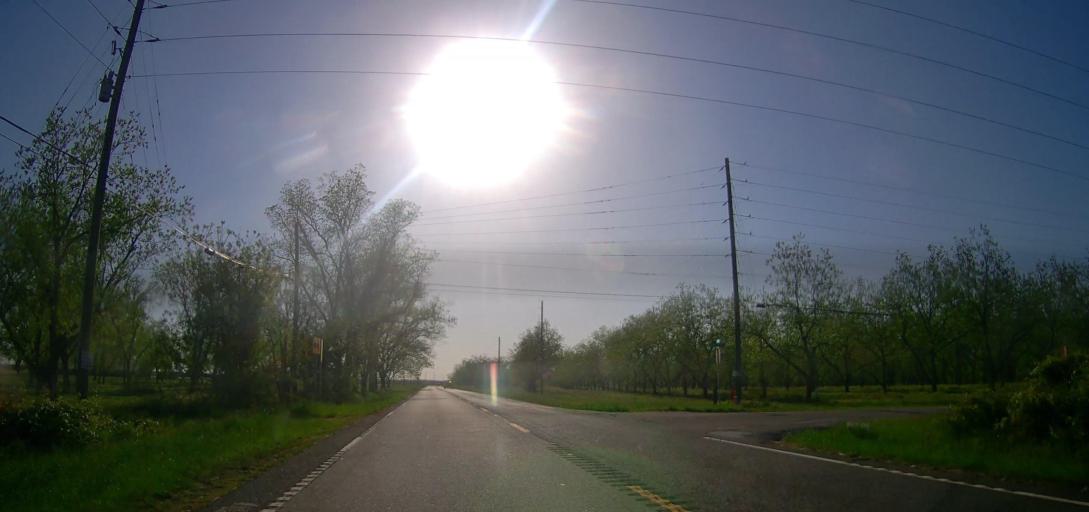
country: US
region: Georgia
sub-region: Houston County
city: Perry
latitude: 32.4399
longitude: -83.8170
